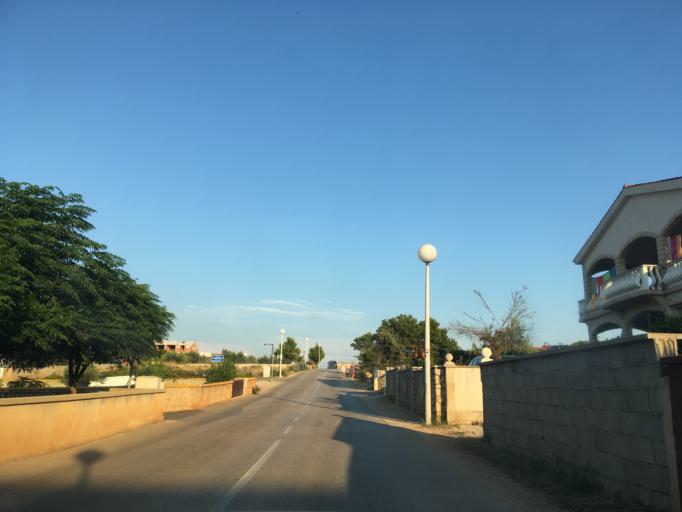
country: HR
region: Zadarska
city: Vir
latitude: 44.3043
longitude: 15.1042
